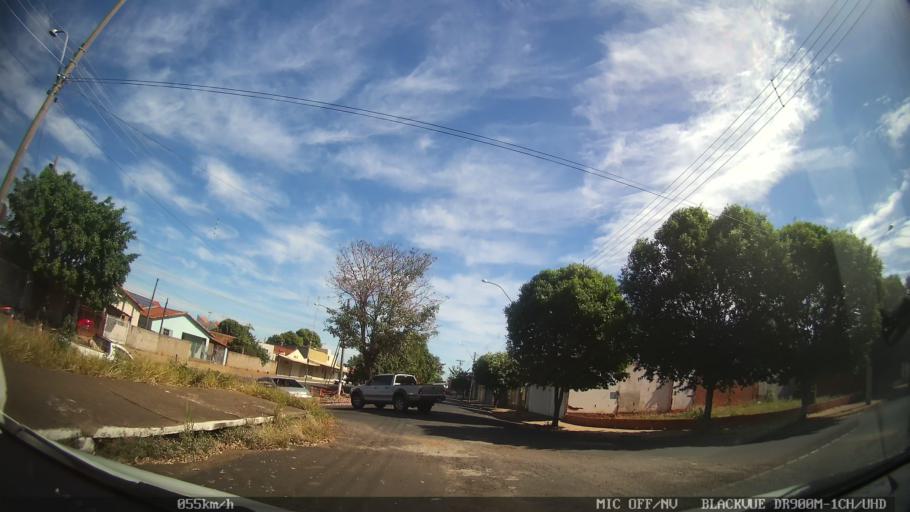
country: BR
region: Sao Paulo
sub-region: Bady Bassitt
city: Bady Bassitt
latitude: -20.8214
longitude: -49.4923
